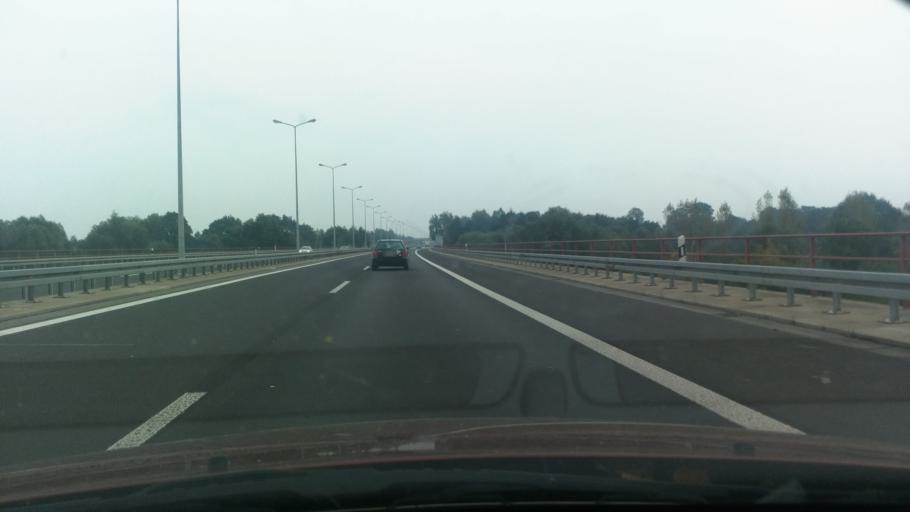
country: DE
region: Saxony
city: Goerlitz
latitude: 51.1820
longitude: 15.0051
